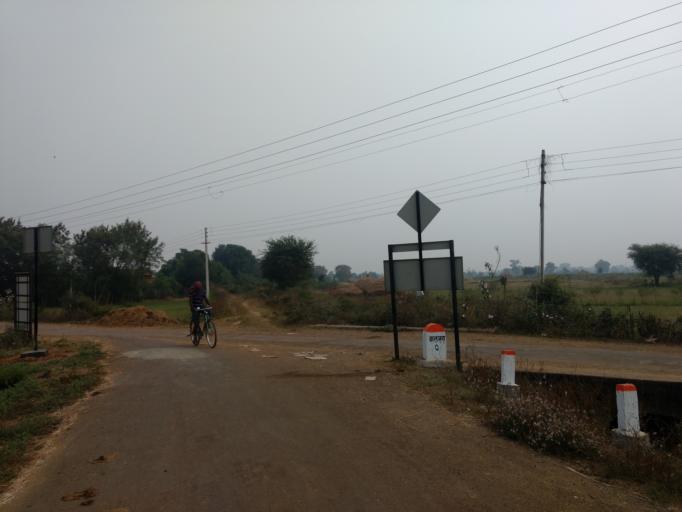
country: IN
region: Maharashtra
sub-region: Chandrapur
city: Mul
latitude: 19.9167
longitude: 79.9464
